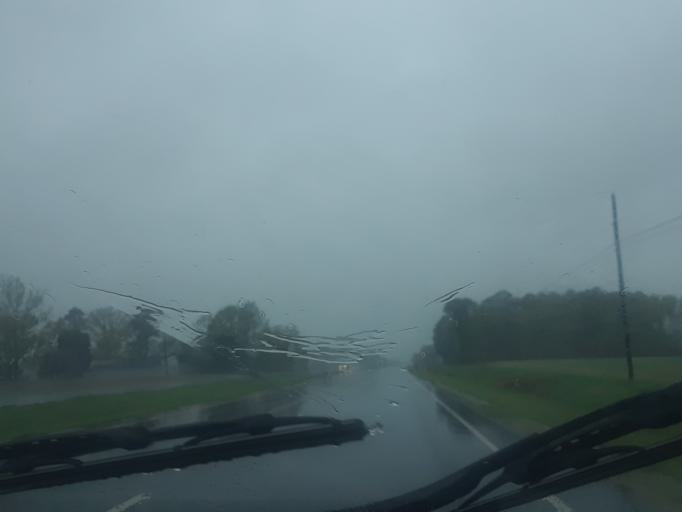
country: US
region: North Carolina
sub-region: Harnett County
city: Erwin
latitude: 35.3602
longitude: -78.6994
